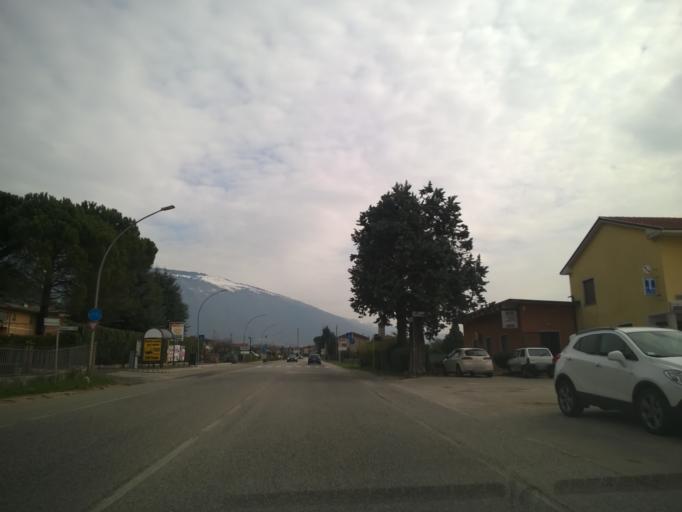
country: IT
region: Veneto
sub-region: Provincia di Vicenza
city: Piovene Rocchette
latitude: 45.7431
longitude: 11.4186
